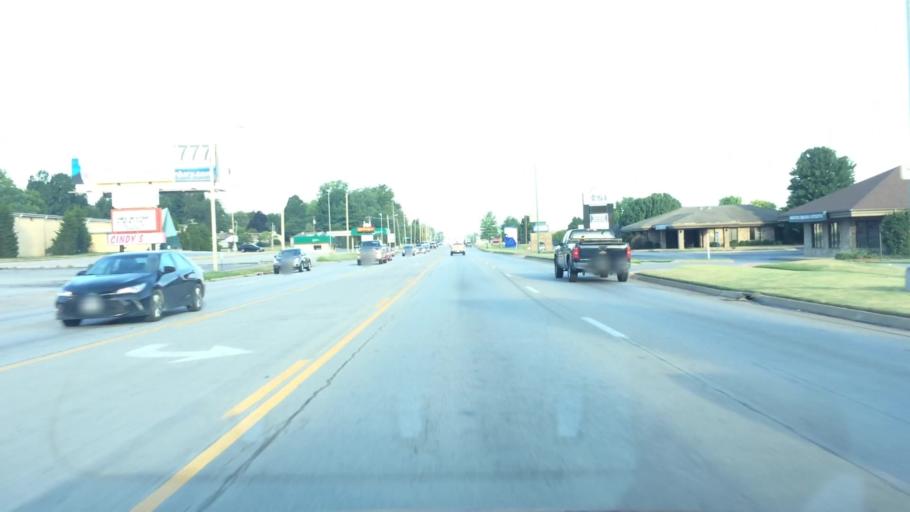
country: US
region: Missouri
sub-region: Greene County
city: Springfield
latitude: 37.1824
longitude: -93.3102
